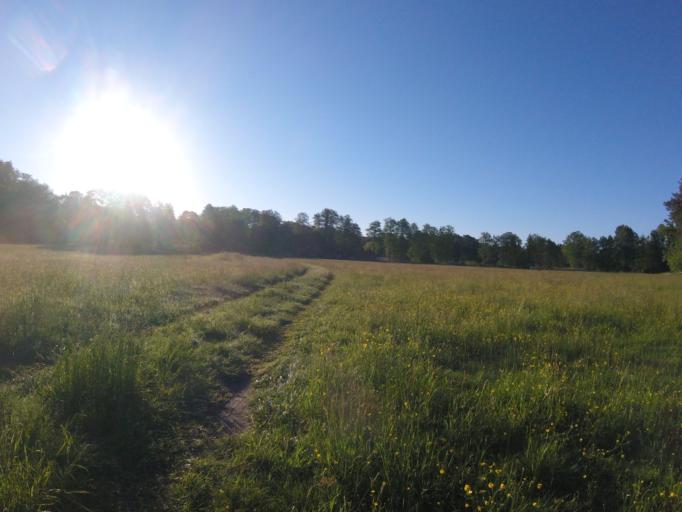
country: DE
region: Brandenburg
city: Bestensee
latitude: 52.2625
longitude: 13.7368
